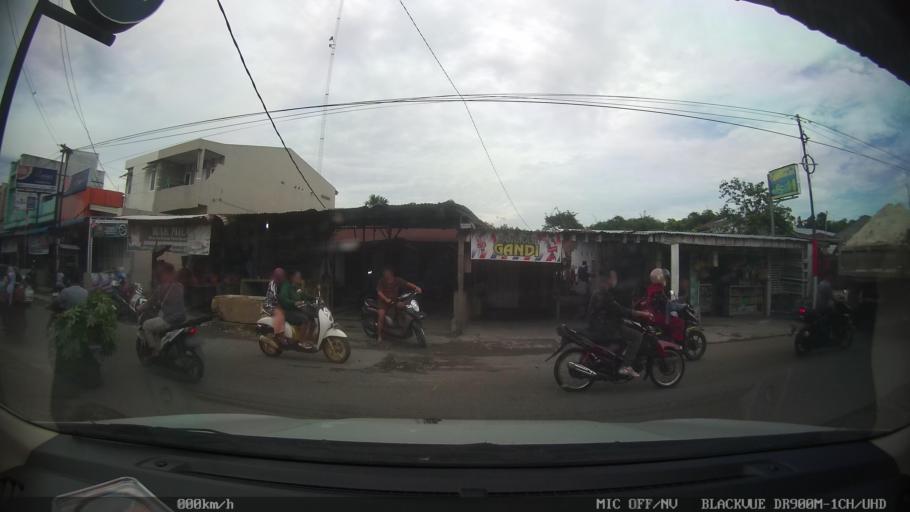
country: ID
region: North Sumatra
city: Sunggal
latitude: 3.6447
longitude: 98.5940
